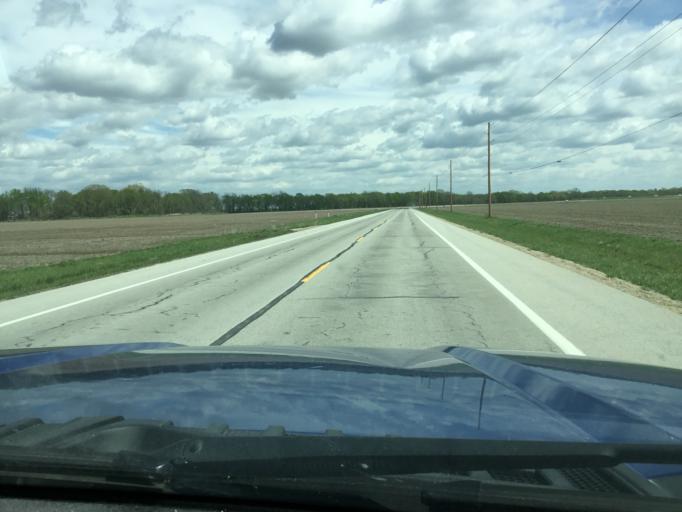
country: US
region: Kansas
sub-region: Douglas County
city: Lawrence
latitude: 38.9136
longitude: -95.2754
